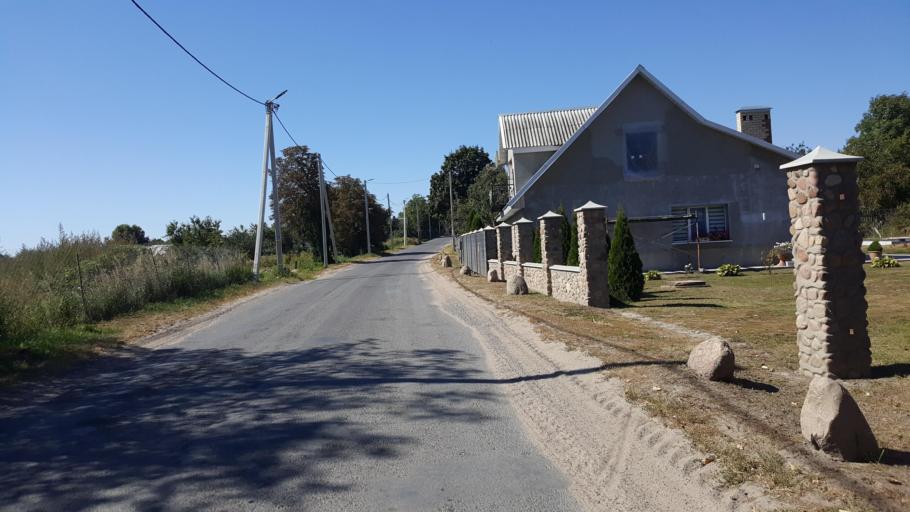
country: BY
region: Brest
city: Vysokaye
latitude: 52.2215
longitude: 23.4408
